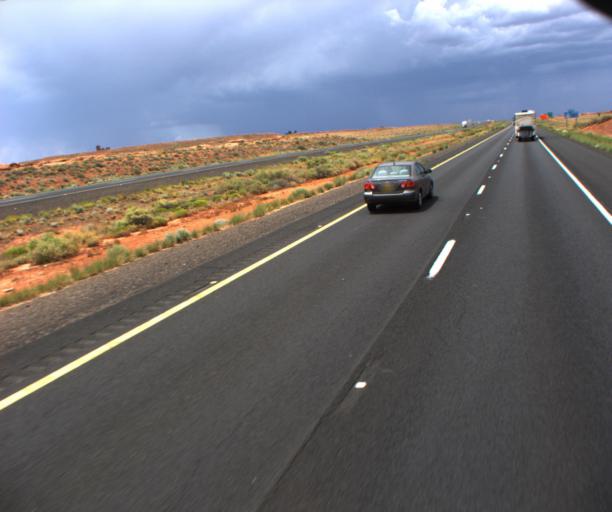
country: US
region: Arizona
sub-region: Coconino County
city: LeChee
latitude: 35.1074
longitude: -111.0125
